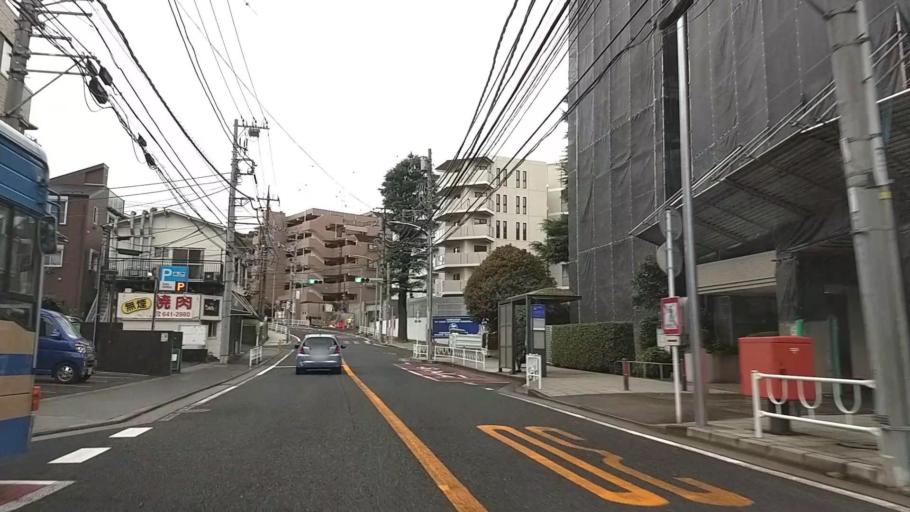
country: JP
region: Kanagawa
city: Yokohama
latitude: 35.4259
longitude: 139.6401
